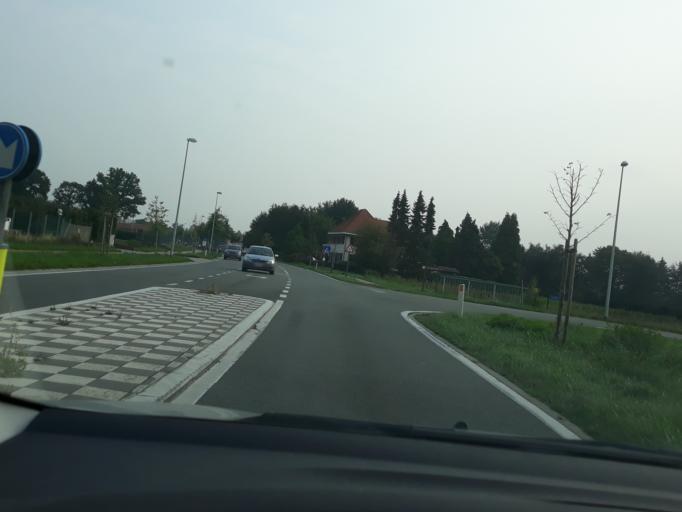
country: BE
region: Flanders
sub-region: Provincie Antwerpen
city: Ravels
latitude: 51.3899
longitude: 4.9949
